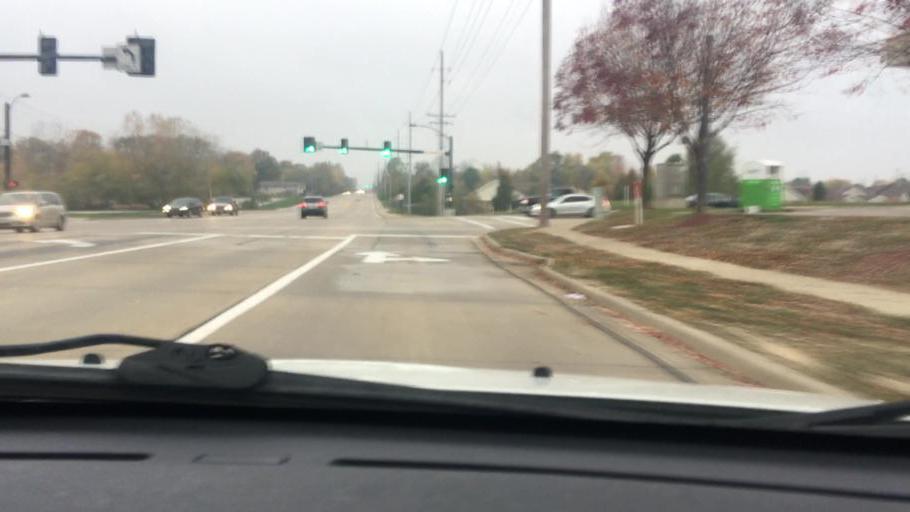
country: US
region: Missouri
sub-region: Saint Charles County
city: O'Fallon
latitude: 38.8218
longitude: -90.6815
